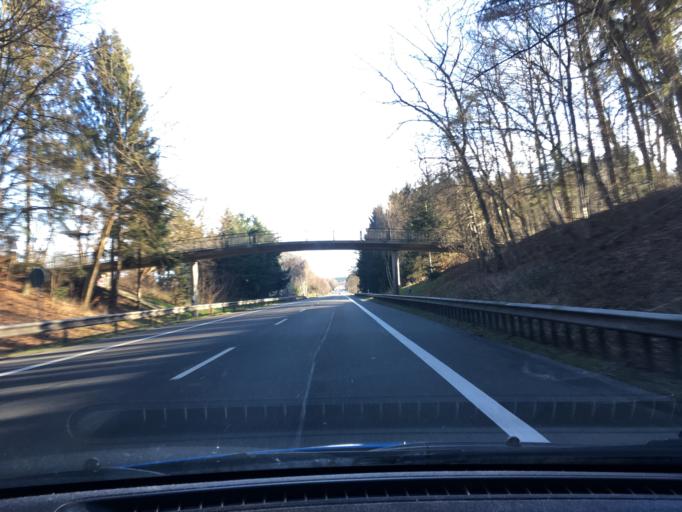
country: DE
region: Lower Saxony
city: Bienenbuttel
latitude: 53.1424
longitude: 10.4767
